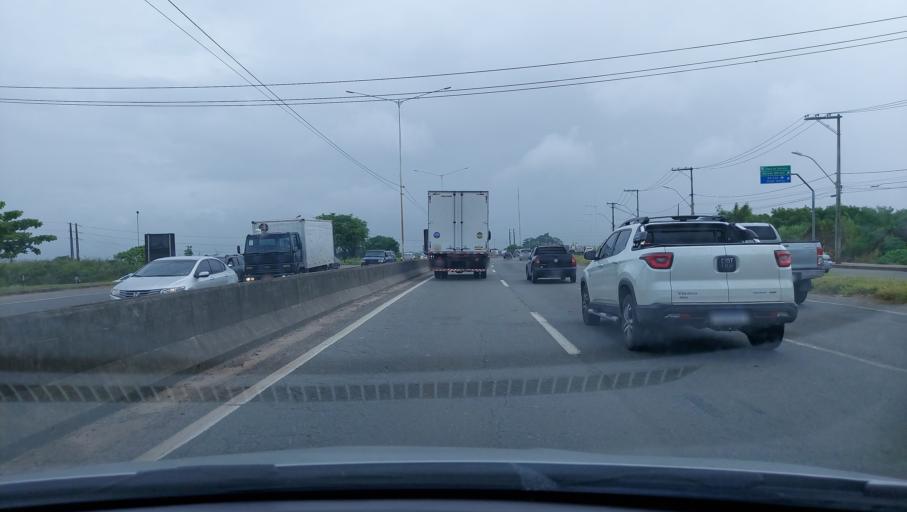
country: BR
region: Bahia
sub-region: Salvador
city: Salvador
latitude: -12.8909
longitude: -38.4450
